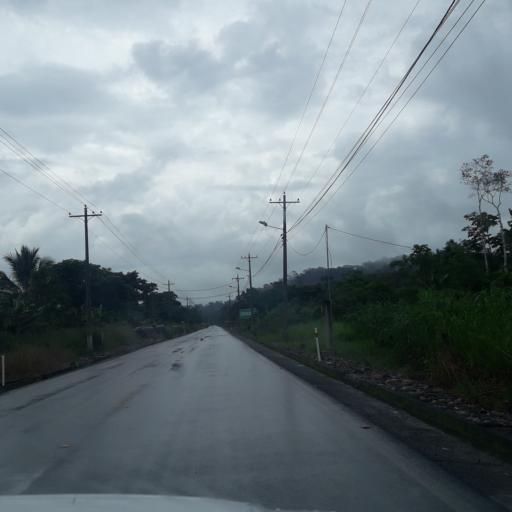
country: EC
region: Napo
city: Tena
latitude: -1.0655
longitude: -77.6449
